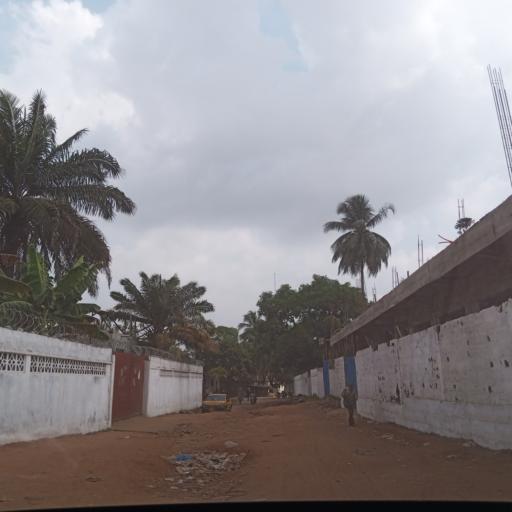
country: LR
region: Montserrado
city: Monrovia
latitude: 6.2890
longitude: -10.6906
